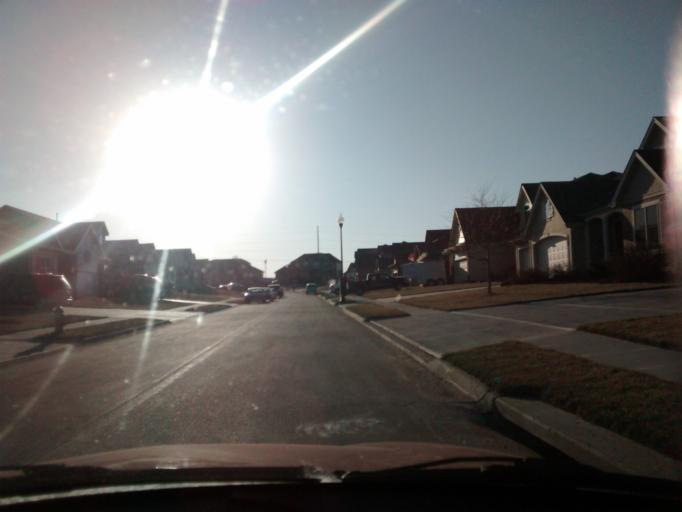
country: US
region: Nebraska
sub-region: Sarpy County
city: Papillion
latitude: 41.1451
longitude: -95.9830
